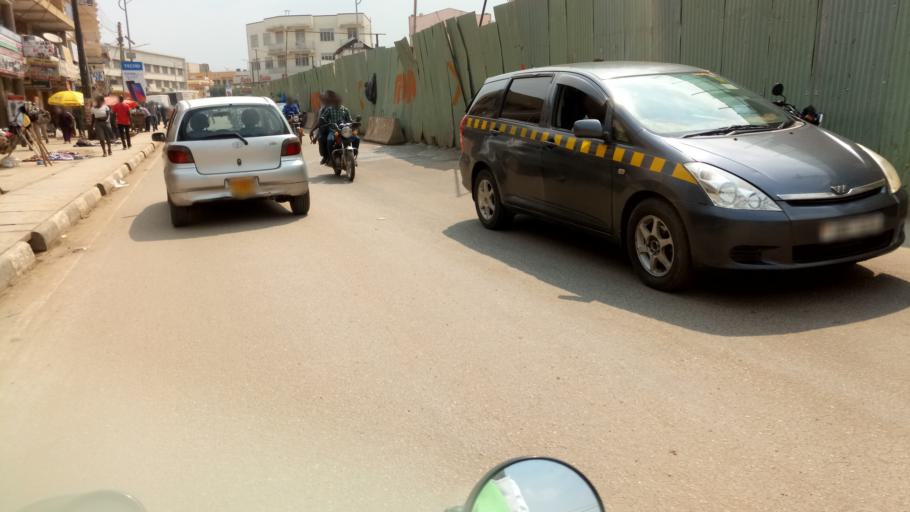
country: UG
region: Western Region
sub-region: Mbarara District
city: Mbarara
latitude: -0.6073
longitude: 30.6632
